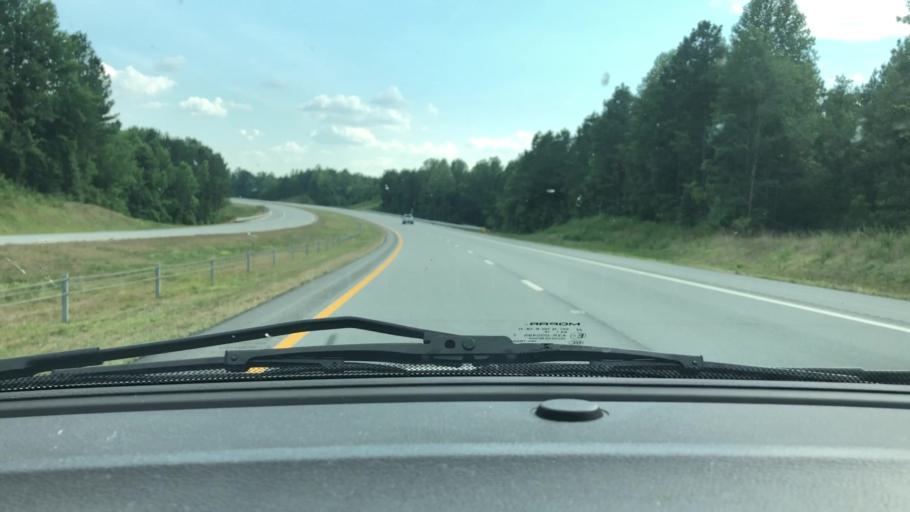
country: US
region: North Carolina
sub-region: Guilford County
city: Oak Ridge
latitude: 36.1638
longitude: -79.9563
